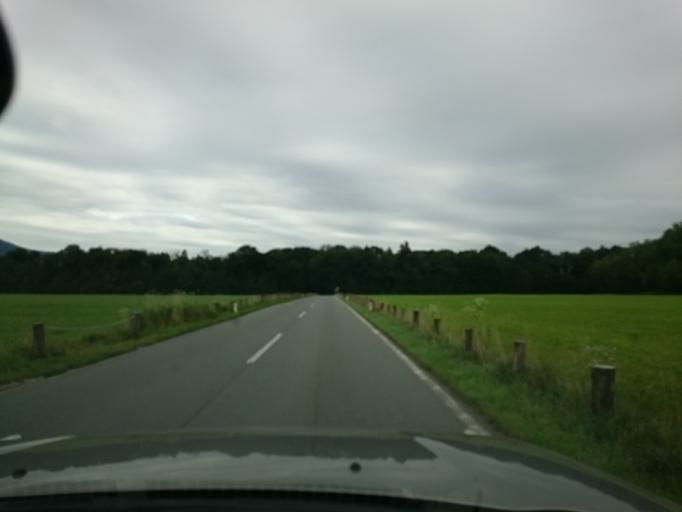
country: AT
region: Salzburg
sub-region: Politischer Bezirk Salzburg-Umgebung
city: Grodig
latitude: 47.7471
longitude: 13.0081
